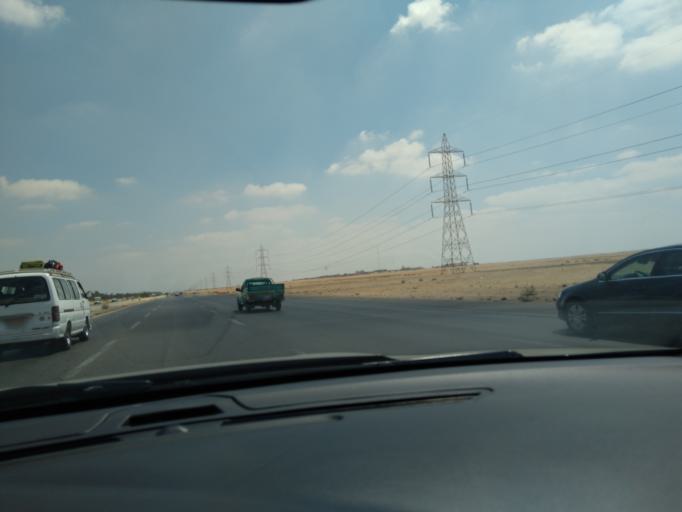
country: EG
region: Al Isma'iliyah
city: At Tall al Kabir
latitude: 30.3843
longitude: 31.9530
